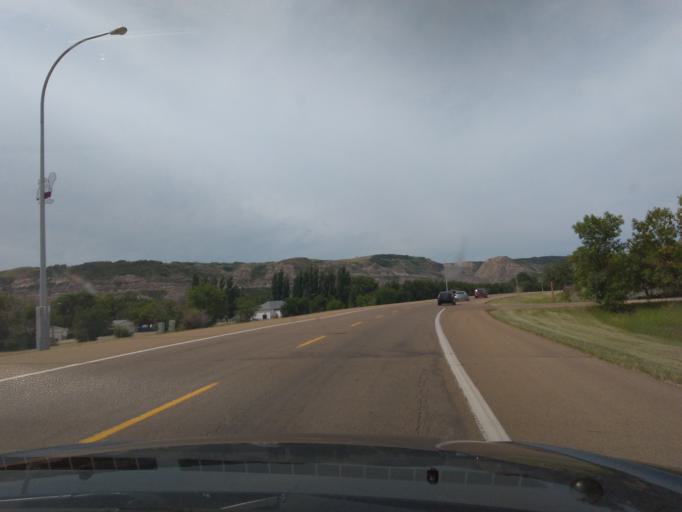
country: CA
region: Alberta
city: Three Hills
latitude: 51.4679
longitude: -112.7498
